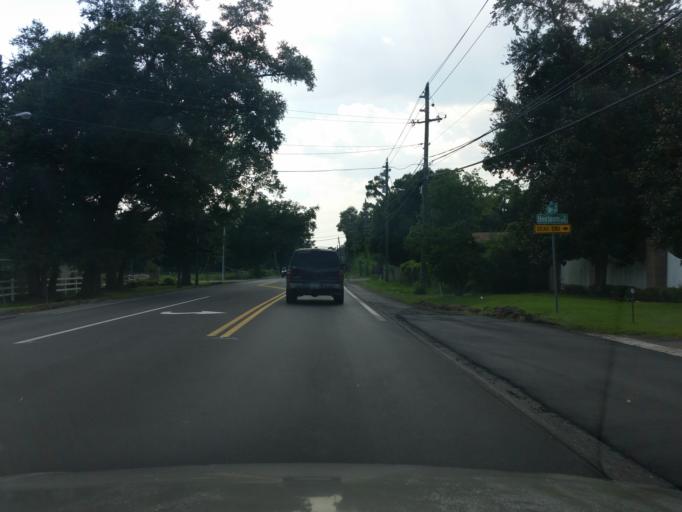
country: US
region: Florida
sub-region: Escambia County
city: Ferry Pass
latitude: 30.5109
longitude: -87.2358
